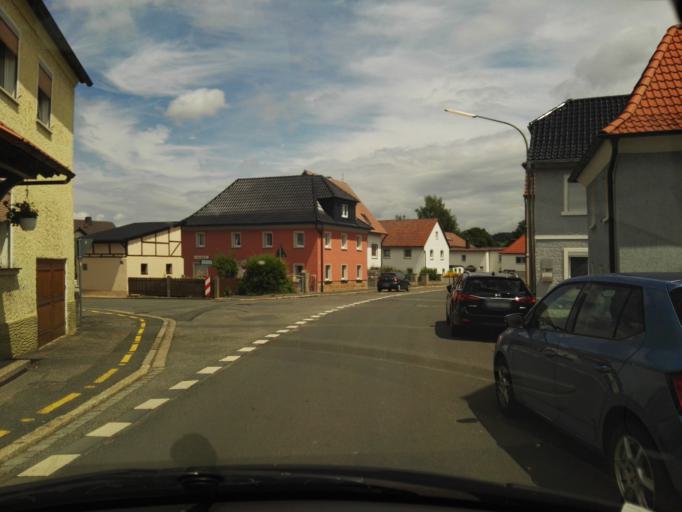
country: DE
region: Bavaria
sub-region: Upper Franconia
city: Altenkunstadt
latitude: 50.1264
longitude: 11.2504
